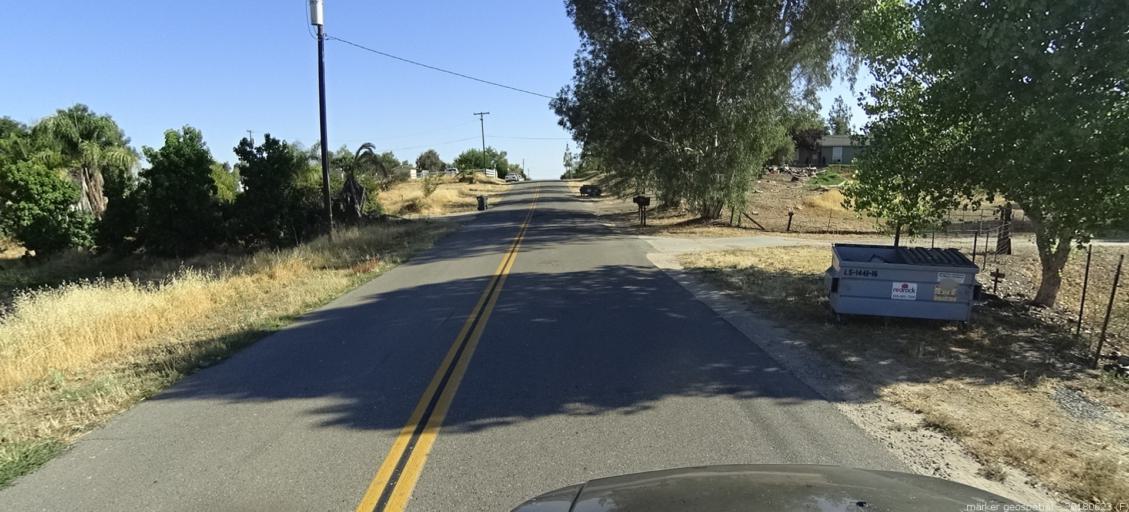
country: US
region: California
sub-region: Madera County
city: Bonadelle Ranchos-Madera Ranchos
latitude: 36.9638
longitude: -119.8015
